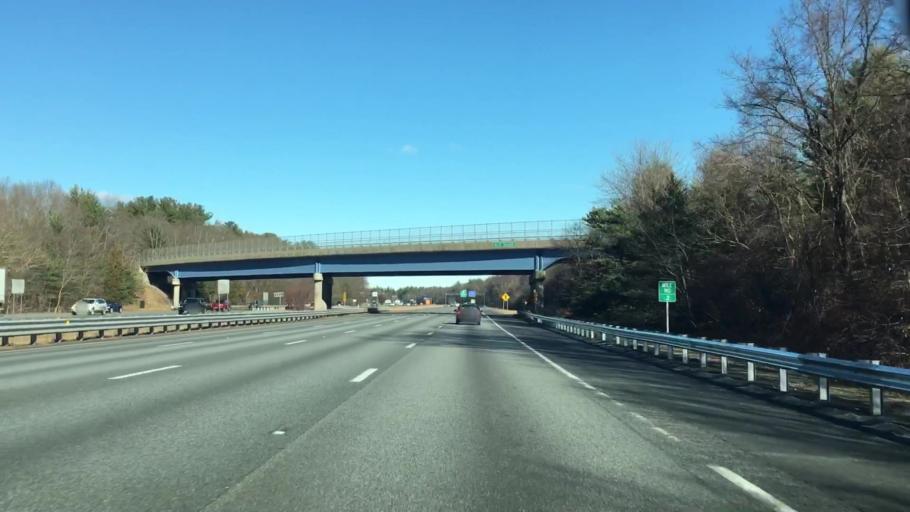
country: US
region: New Hampshire
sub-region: Rockingham County
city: Seabrook
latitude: 42.8727
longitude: -70.8876
